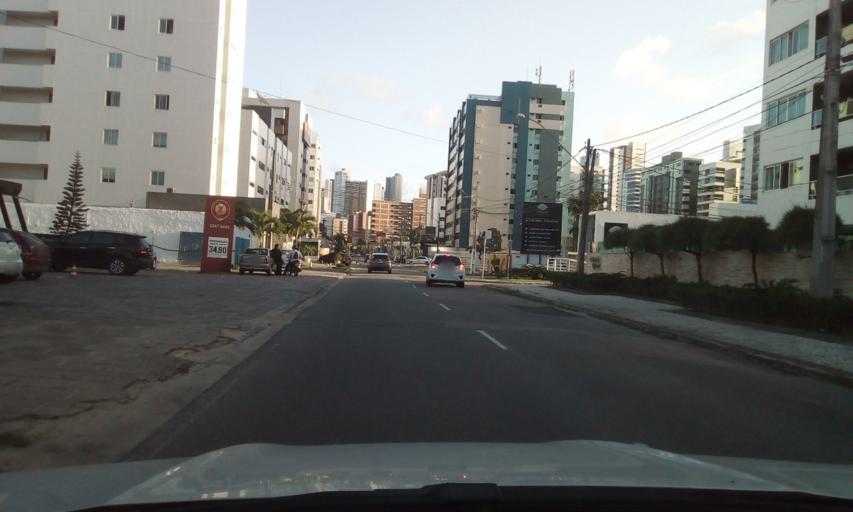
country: BR
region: Paraiba
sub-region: Joao Pessoa
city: Joao Pessoa
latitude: -7.1169
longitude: -34.8261
